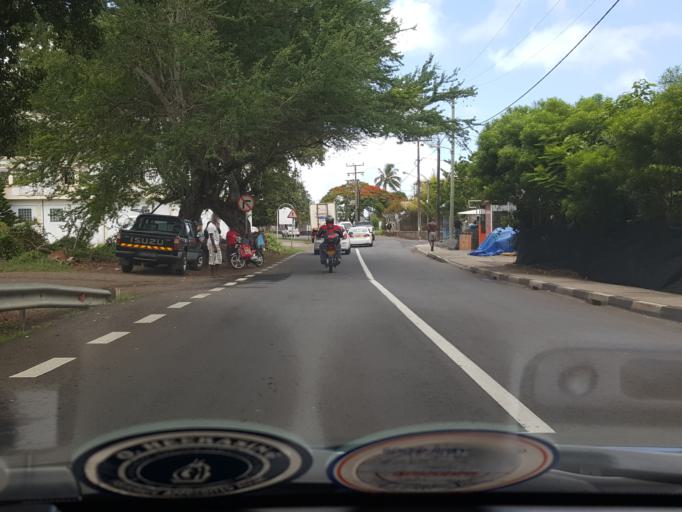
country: MU
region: Black River
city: Petite Case Noyale
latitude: -20.3919
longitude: 57.3804
